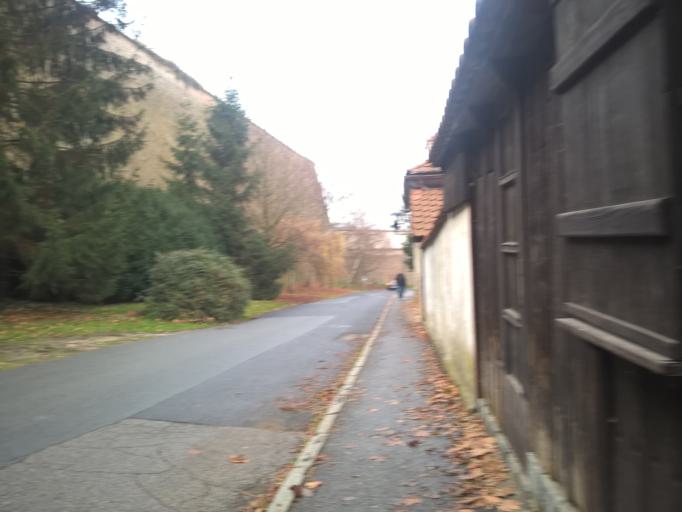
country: CZ
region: Praha
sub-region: Praha 1
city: Mala Strana
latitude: 50.0850
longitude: 14.3881
